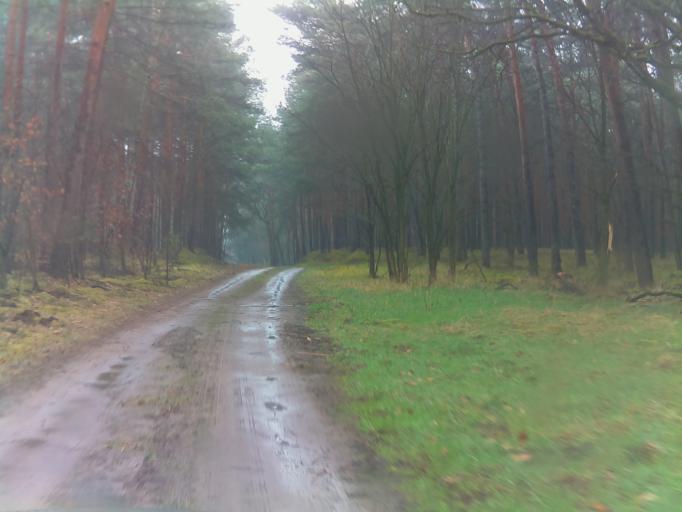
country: DE
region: Brandenburg
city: Jamlitz
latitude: 52.0440
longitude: 14.3644
